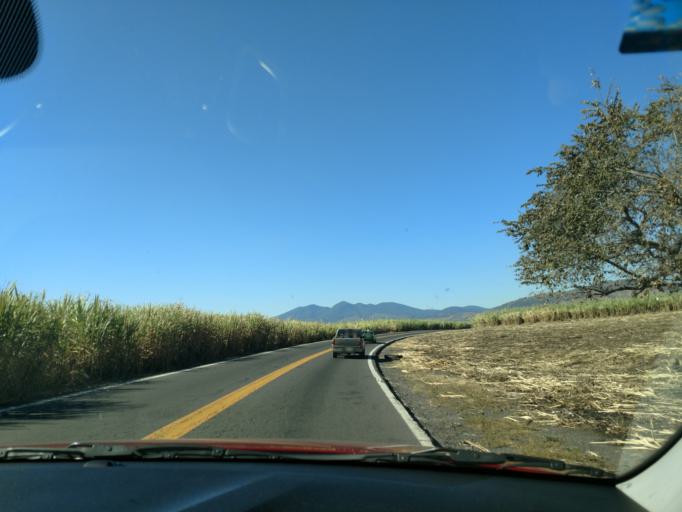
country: MX
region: Nayarit
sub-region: Ahuacatlan
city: Ahuacatlan
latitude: 21.1330
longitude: -104.6058
